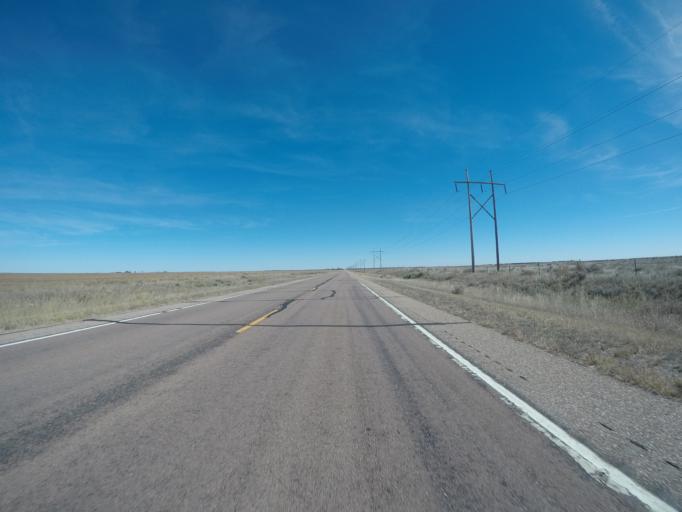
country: US
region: Colorado
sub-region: Yuma County
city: Yuma
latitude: 39.6550
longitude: -102.7885
